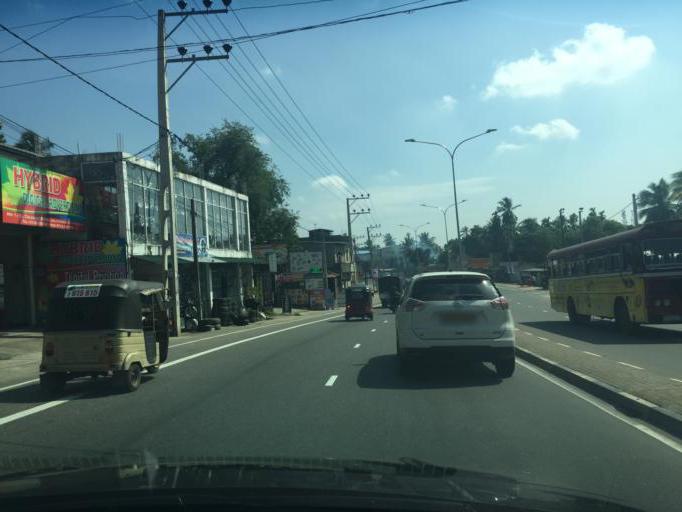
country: LK
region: Western
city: Maharagama
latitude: 6.8128
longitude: 79.9199
